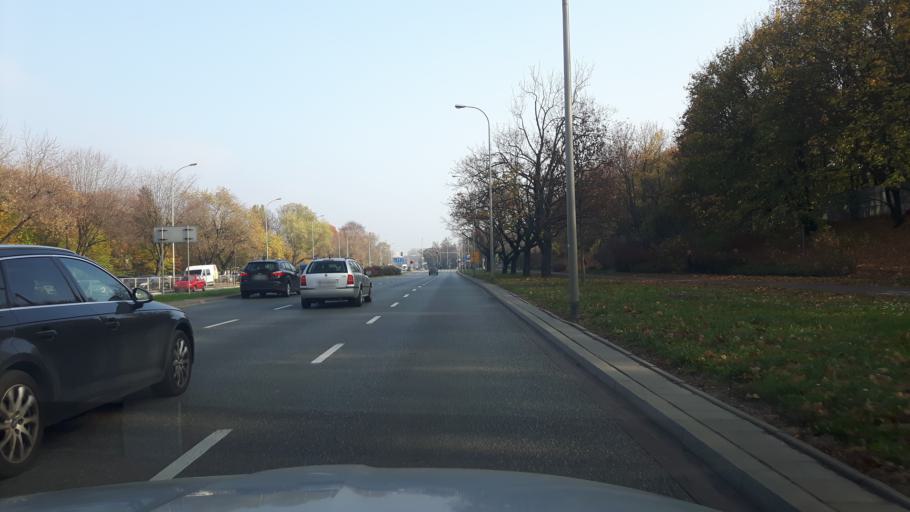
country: PL
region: Masovian Voivodeship
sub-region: Warszawa
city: Ochota
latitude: 52.1973
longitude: 20.9895
